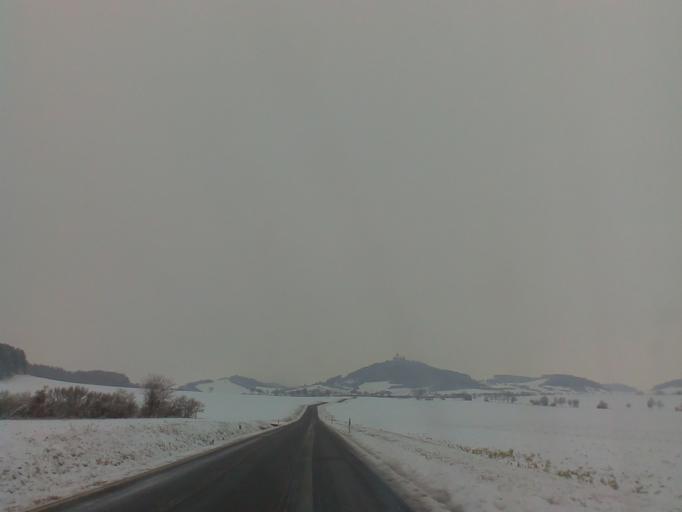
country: DE
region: Thuringia
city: Arnstadt
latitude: 50.8441
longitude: 10.9085
